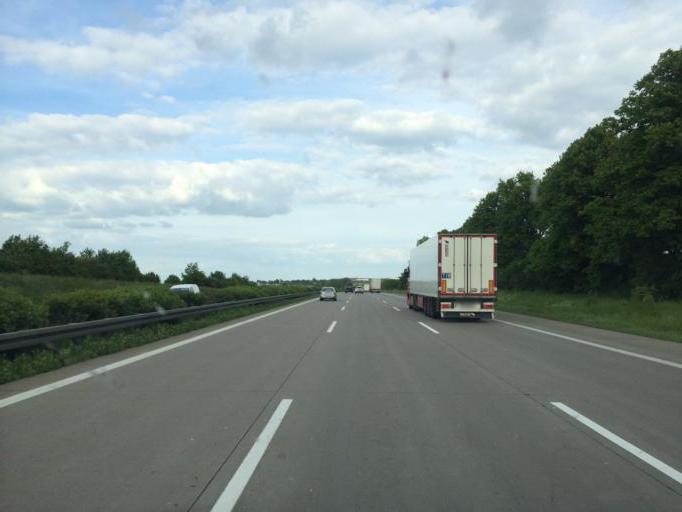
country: DE
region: Saxony-Anhalt
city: Eichenbarleben
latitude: 52.1880
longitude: 11.4169
